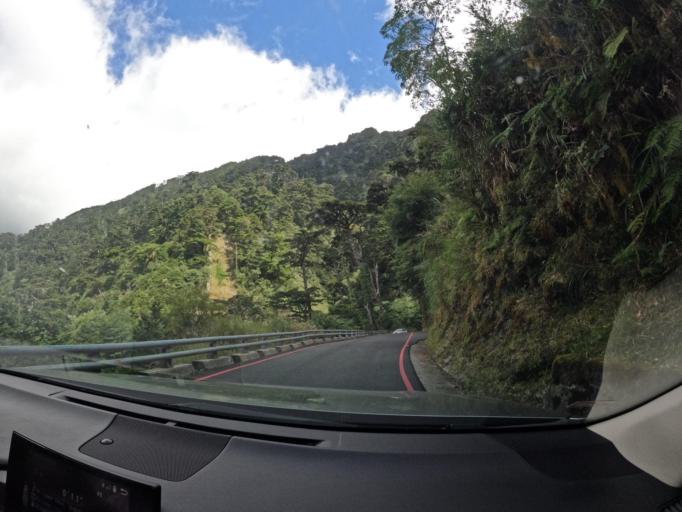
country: TW
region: Taiwan
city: Yujing
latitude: 23.2594
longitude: 120.9448
